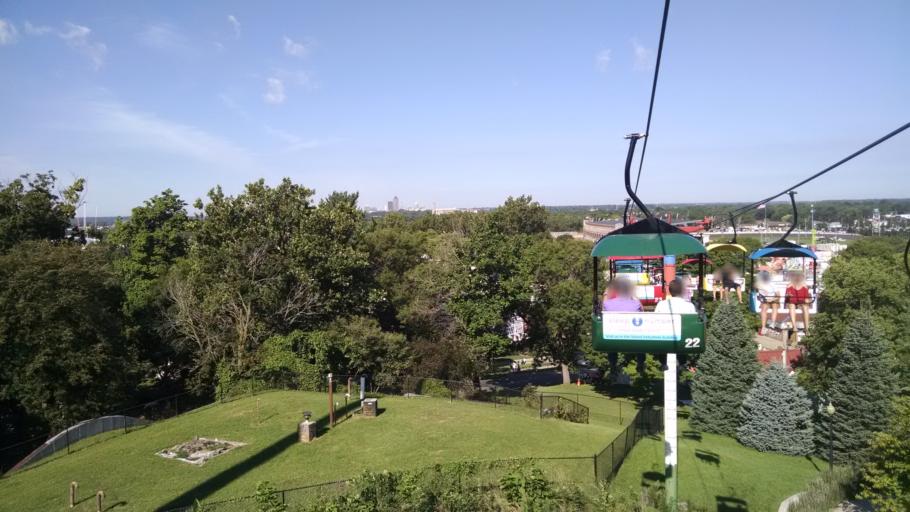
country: US
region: Iowa
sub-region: Polk County
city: Pleasant Hill
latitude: 41.5955
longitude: -93.5492
